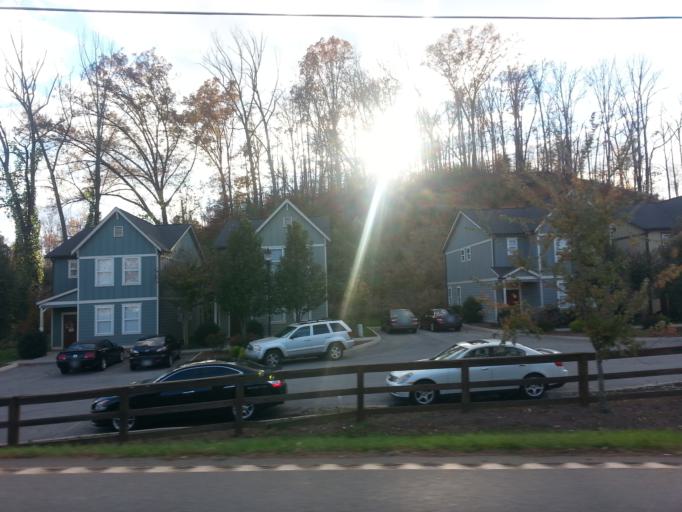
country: US
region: Tennessee
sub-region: Knox County
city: Knoxville
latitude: 35.9352
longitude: -83.9330
